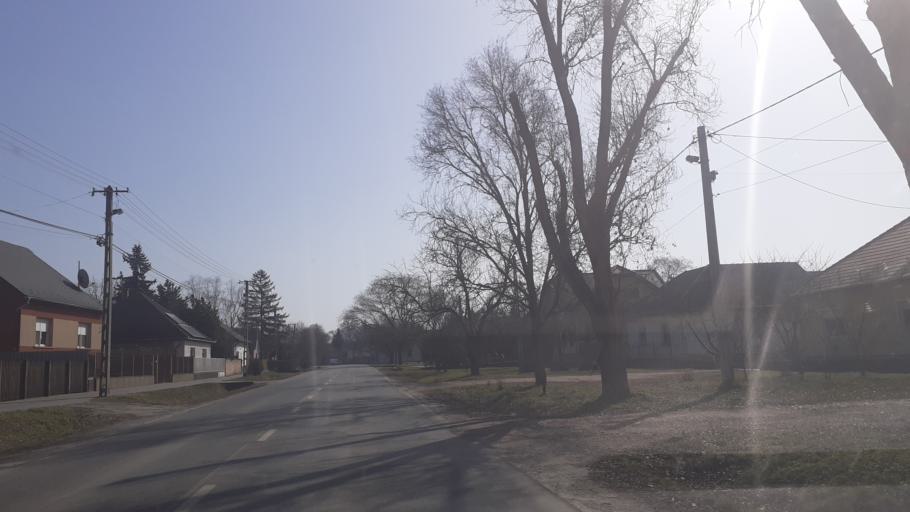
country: HU
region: Pest
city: Dabas
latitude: 47.1685
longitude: 19.3257
